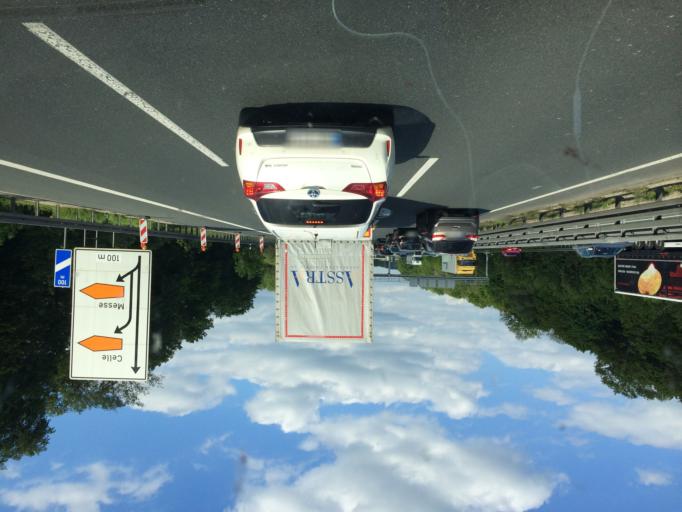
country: DE
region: Lower Saxony
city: Isernhagen Farster Bauerschaft
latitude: 52.3986
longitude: 9.8848
